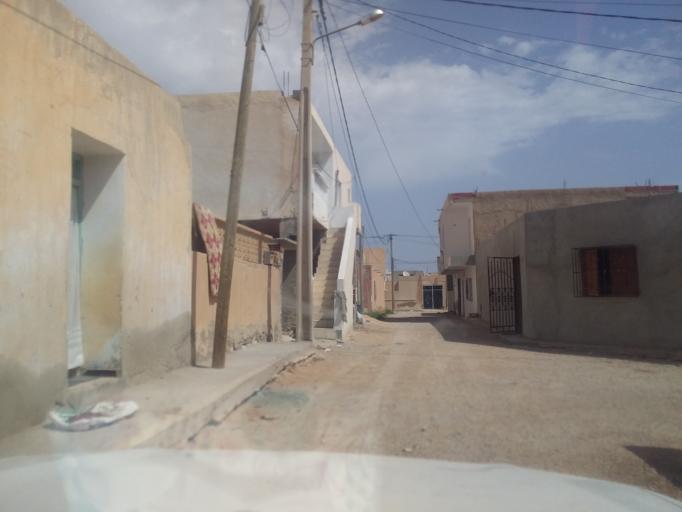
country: TN
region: Madanin
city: Medenine
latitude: 33.5827
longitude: 10.3198
